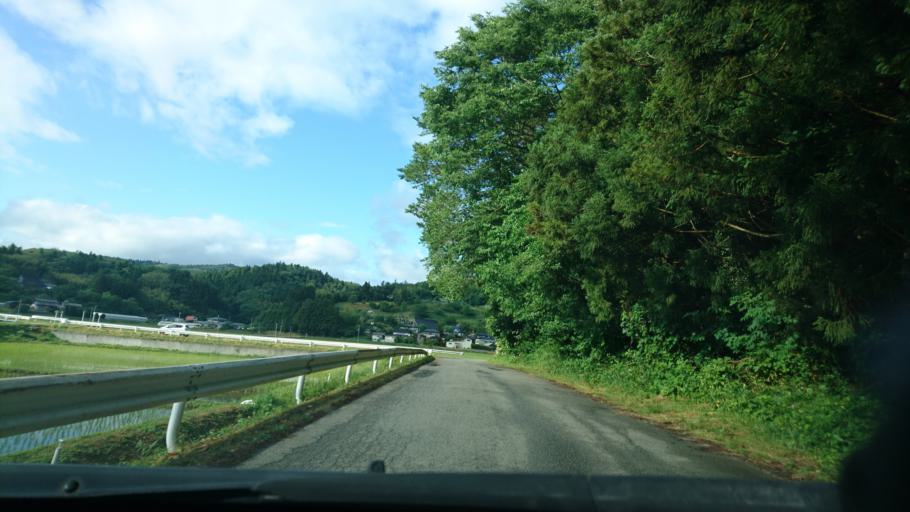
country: JP
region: Iwate
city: Ichinoseki
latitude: 38.8555
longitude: 141.2833
